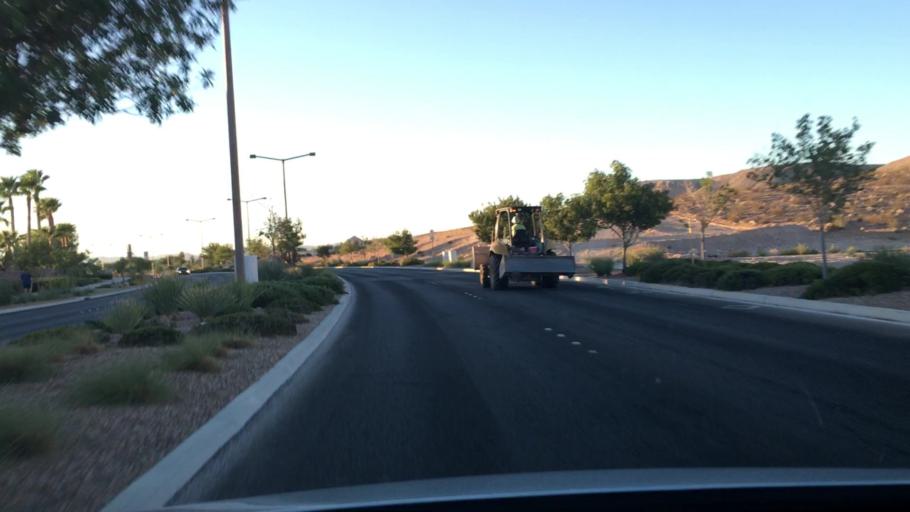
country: US
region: Nevada
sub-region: Clark County
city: Summerlin South
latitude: 36.1025
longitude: -115.3275
